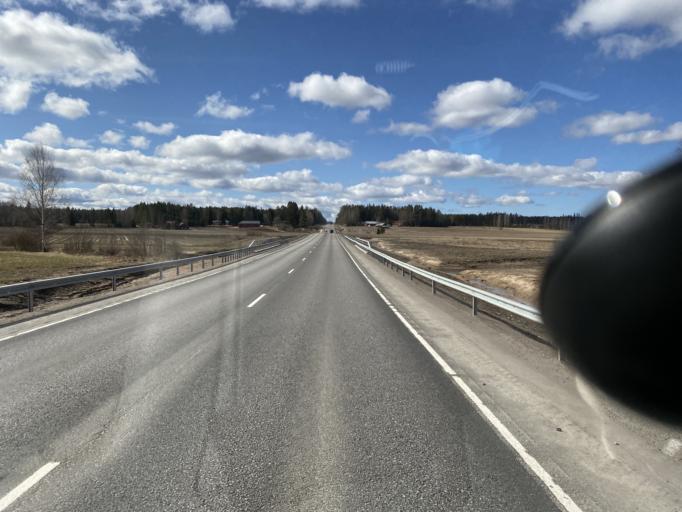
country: FI
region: Satakunta
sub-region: Rauma
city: Koeylioe
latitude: 61.1542
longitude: 22.2662
